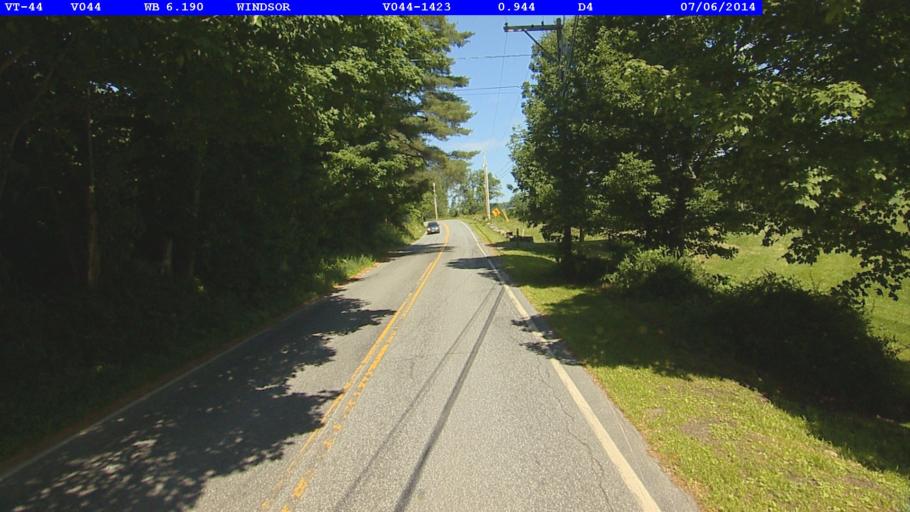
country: US
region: Vermont
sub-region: Windsor County
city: Windsor
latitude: 43.4647
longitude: -72.4349
